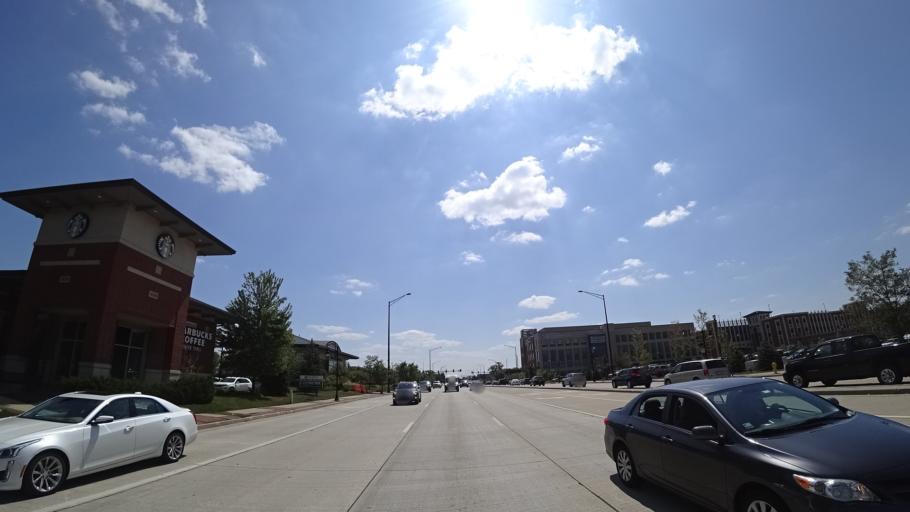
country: US
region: Illinois
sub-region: Cook County
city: Orland Park
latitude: 41.6322
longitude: -87.8538
